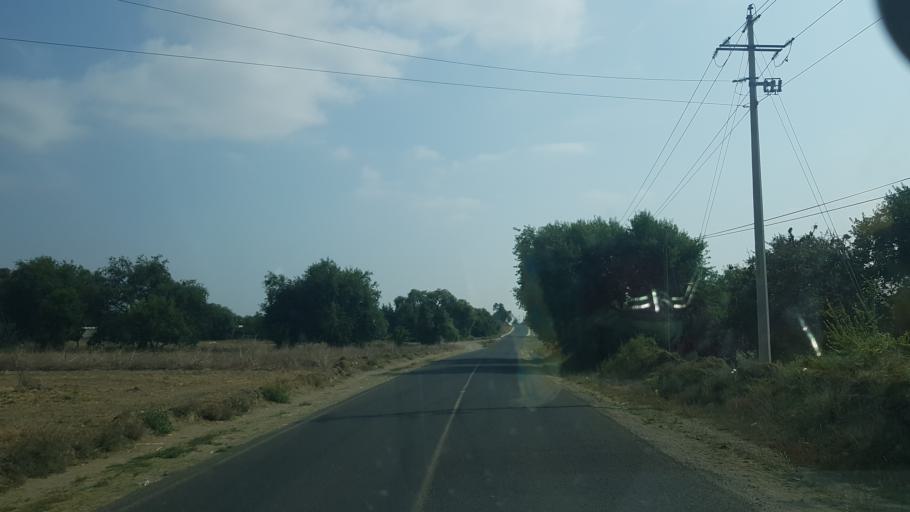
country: MX
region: Puebla
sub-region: Huejotzingo
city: San Juan Pancoac
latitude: 19.1275
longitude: -98.4201
